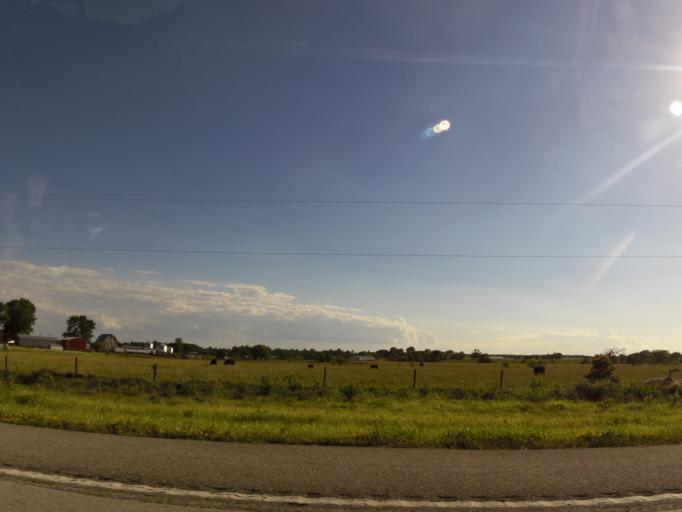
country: US
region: Missouri
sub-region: Pike County
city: Bowling Green
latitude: 39.2916
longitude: -91.1086
